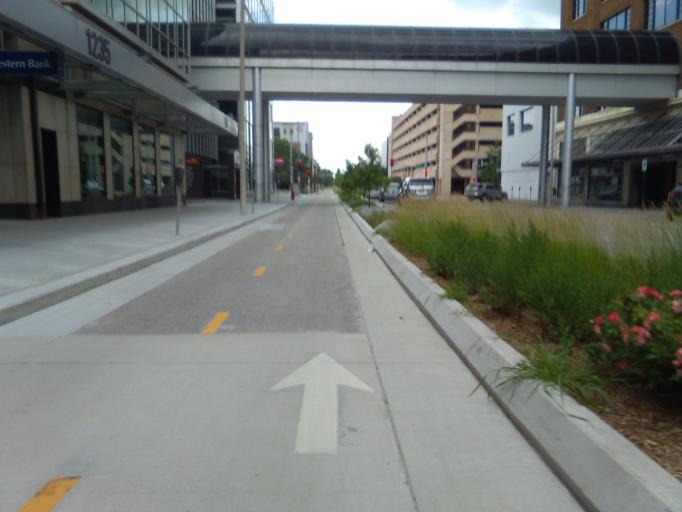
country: US
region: Nebraska
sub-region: Lancaster County
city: Lincoln
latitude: 40.8125
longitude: -96.7029
